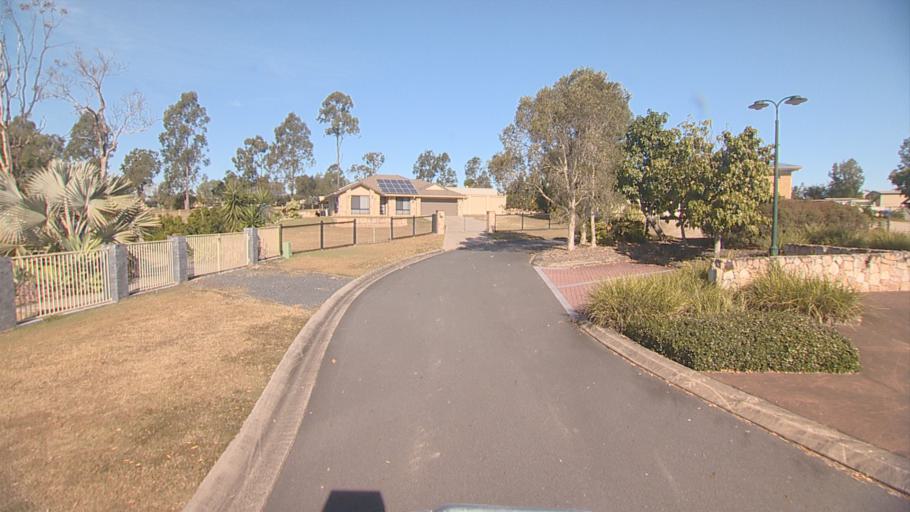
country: AU
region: Queensland
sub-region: Logan
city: North Maclean
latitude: -27.7993
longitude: 152.9639
